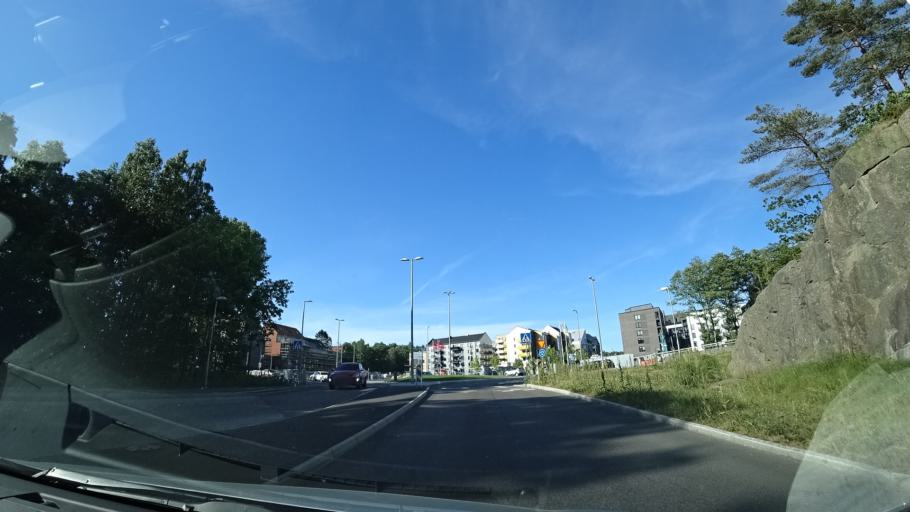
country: SE
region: Vaestra Goetaland
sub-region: Goteborg
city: Billdal
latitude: 57.5978
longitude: 11.9489
